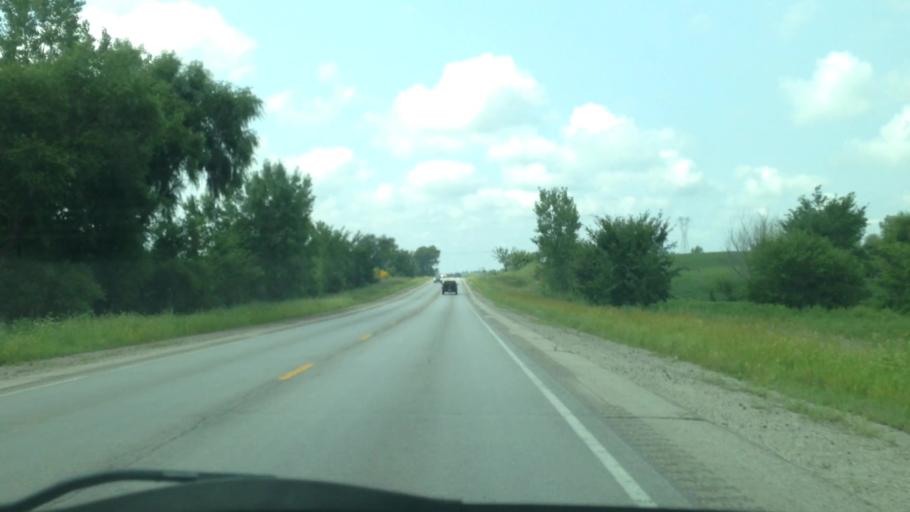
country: US
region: Iowa
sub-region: Benton County
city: Walford
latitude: 41.8908
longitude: -91.8168
